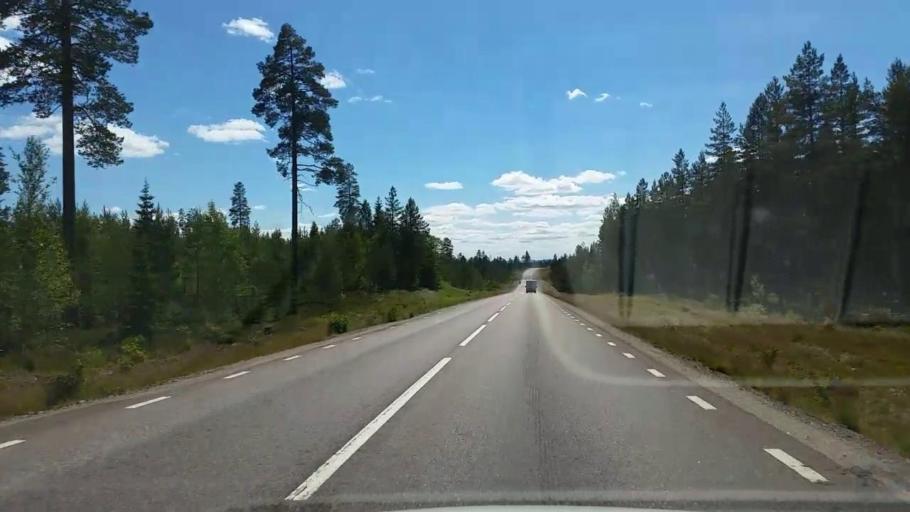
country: SE
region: Gaevleborg
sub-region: Bollnas Kommun
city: Vittsjo
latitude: 61.1082
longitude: 15.8605
